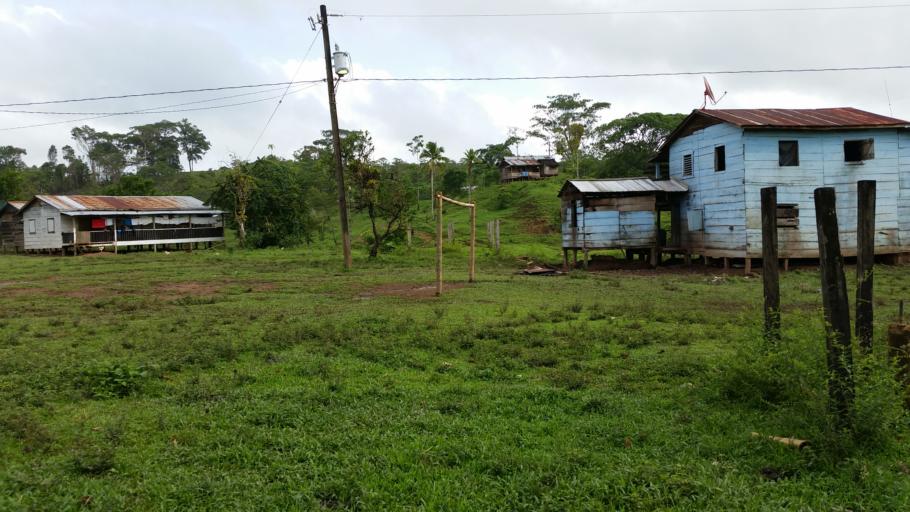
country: NI
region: Atlantico Norte (RAAN)
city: Bonanza
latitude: 14.0913
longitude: -84.6824
